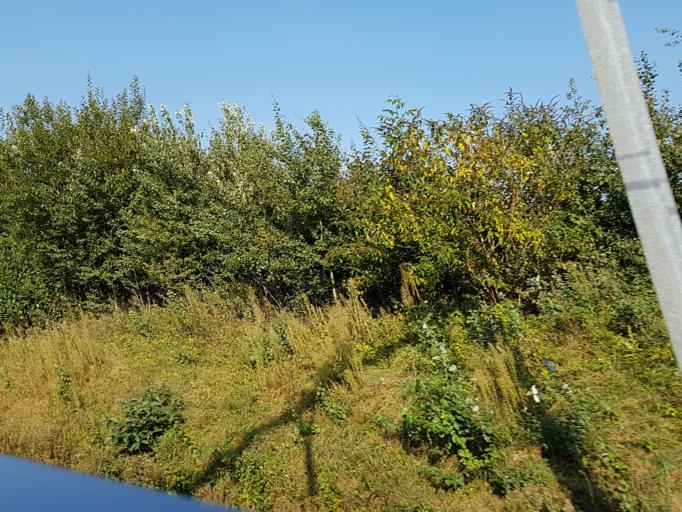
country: BE
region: Flanders
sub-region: Provincie Vlaams-Brabant
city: Diegem
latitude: 50.8947
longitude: 4.4113
